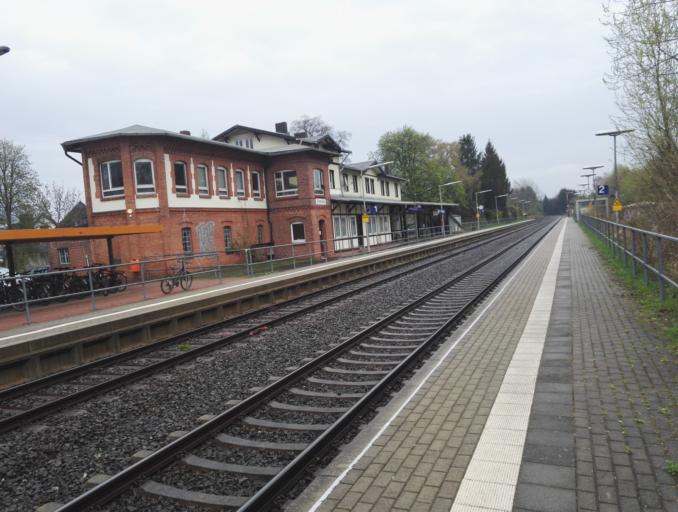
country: DE
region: Lower Saxony
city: Holle
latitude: 52.0970
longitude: 10.1430
